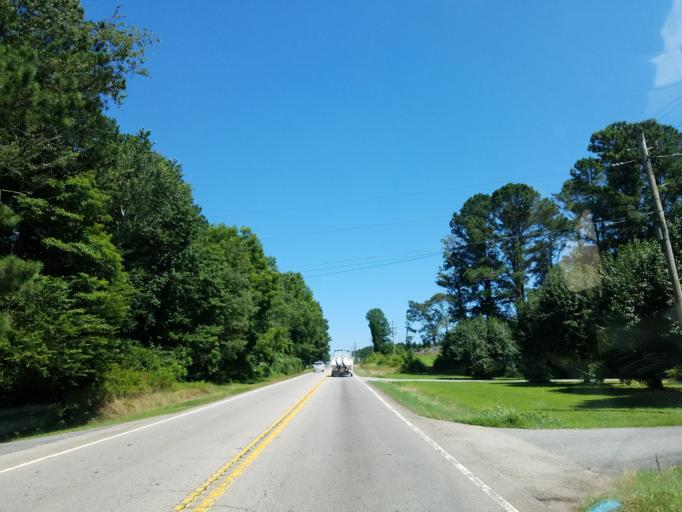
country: US
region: Georgia
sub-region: Forsyth County
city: Cumming
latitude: 34.2603
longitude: -84.0788
